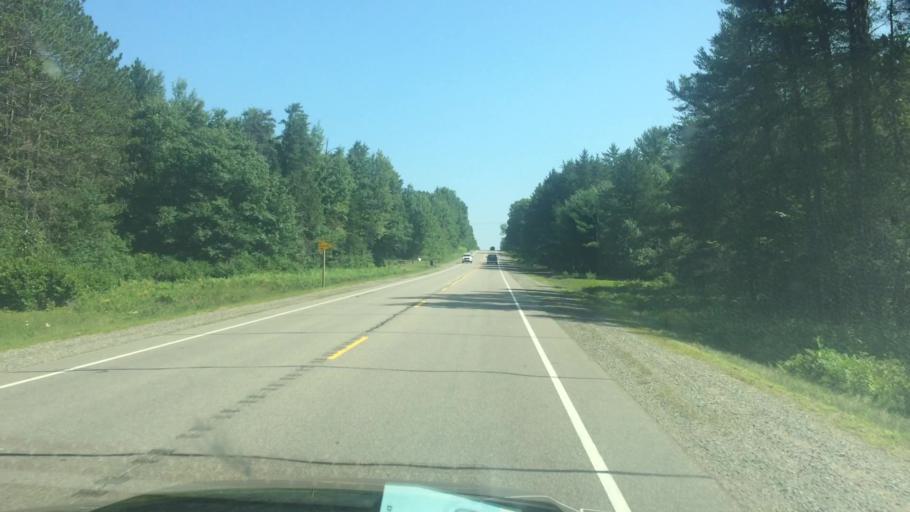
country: US
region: Wisconsin
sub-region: Lincoln County
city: Tomahawk
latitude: 45.5566
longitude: -89.6518
